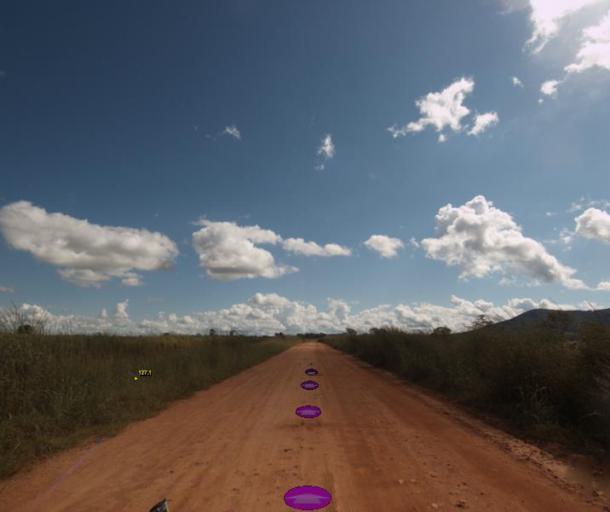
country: BR
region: Goias
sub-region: Jaragua
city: Jaragua
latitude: -15.8321
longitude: -49.2606
